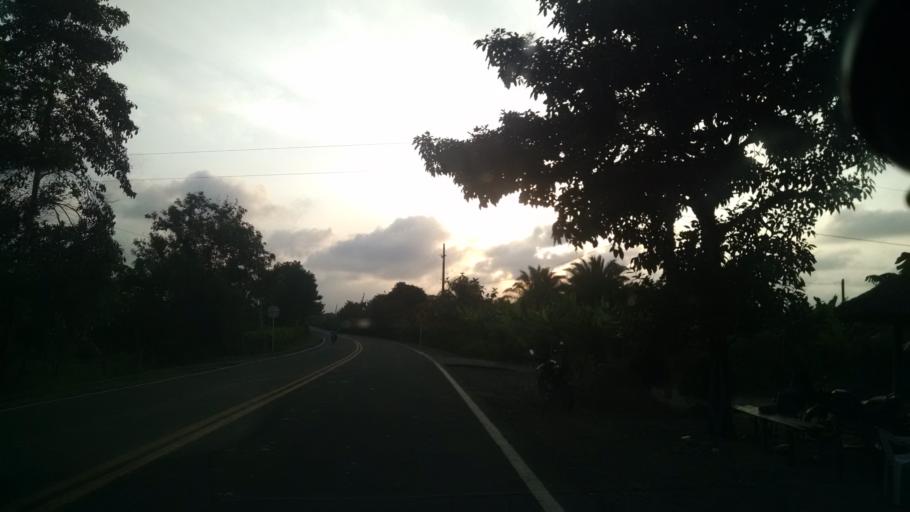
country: CO
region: Antioquia
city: San Juan de Uraba
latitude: 8.7238
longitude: -76.5925
